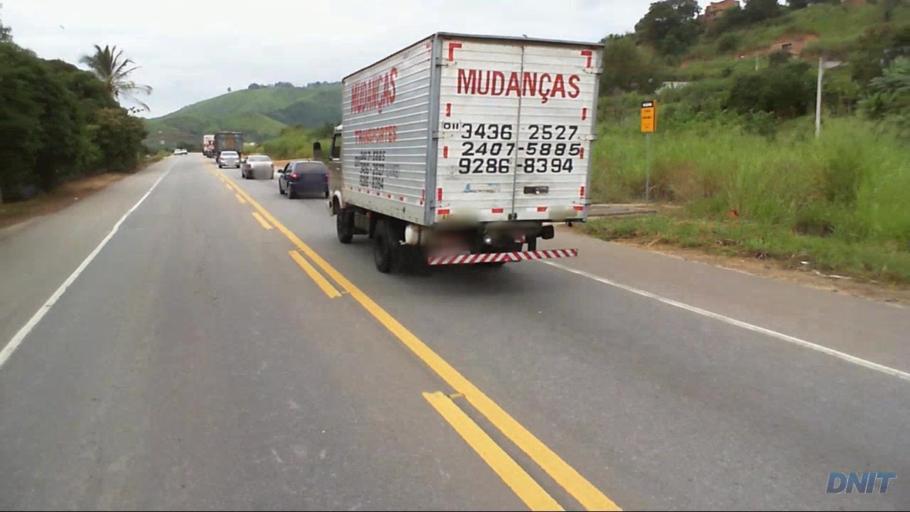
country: BR
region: Minas Gerais
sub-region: Coronel Fabriciano
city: Coronel Fabriciano
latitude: -19.5309
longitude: -42.6202
